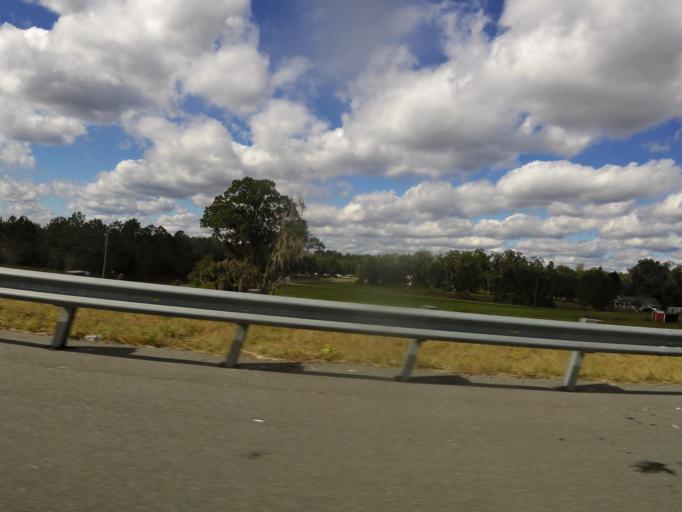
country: US
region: Florida
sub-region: Bradford County
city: Starke
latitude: 29.9634
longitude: -82.1329
